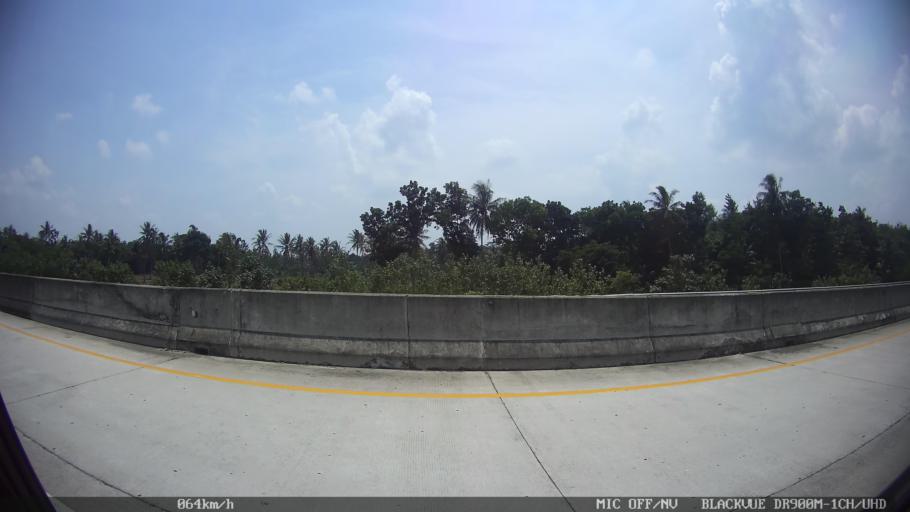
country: ID
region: Lampung
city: Natar
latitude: -5.3037
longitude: 105.2438
